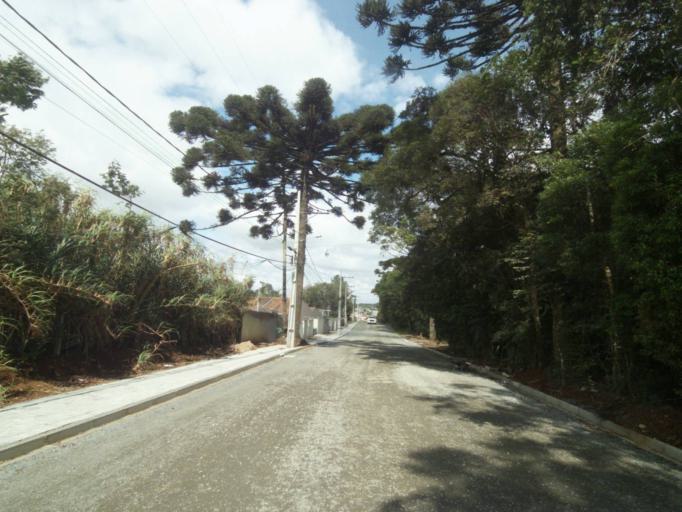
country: BR
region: Parana
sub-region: Campina Grande Do Sul
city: Campina Grande do Sul
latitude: -25.3335
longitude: -49.0709
